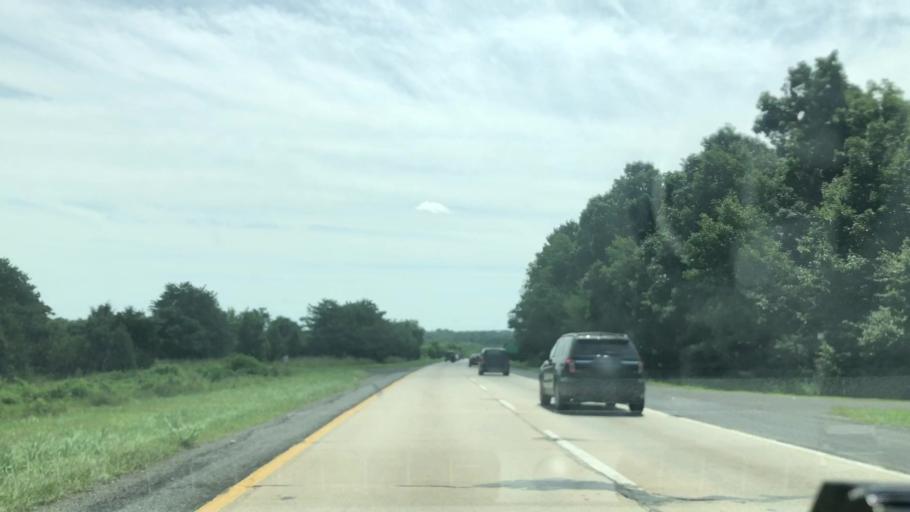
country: US
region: Pennsylvania
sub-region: Montgomery County
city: Audubon
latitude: 40.1418
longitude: -75.4530
